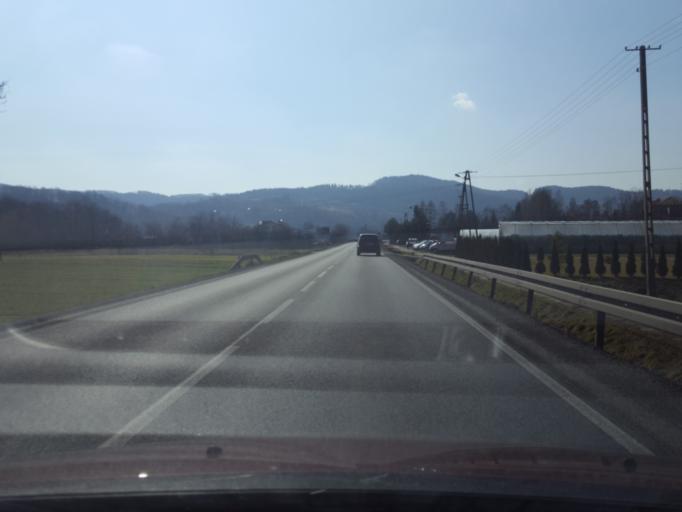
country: PL
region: Lesser Poland Voivodeship
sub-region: Powiat brzeski
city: Czchow
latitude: 49.8273
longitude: 20.6782
